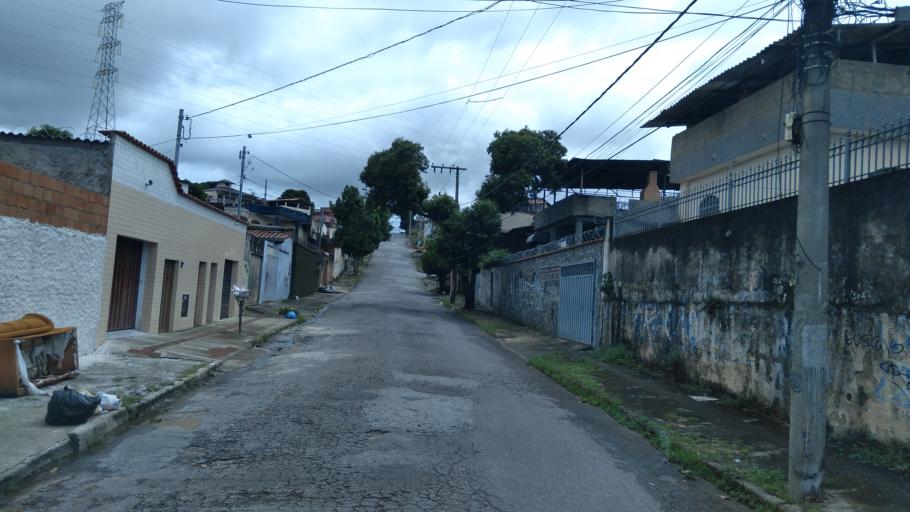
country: BR
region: Minas Gerais
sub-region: Belo Horizonte
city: Belo Horizonte
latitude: -19.8915
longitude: -43.9003
